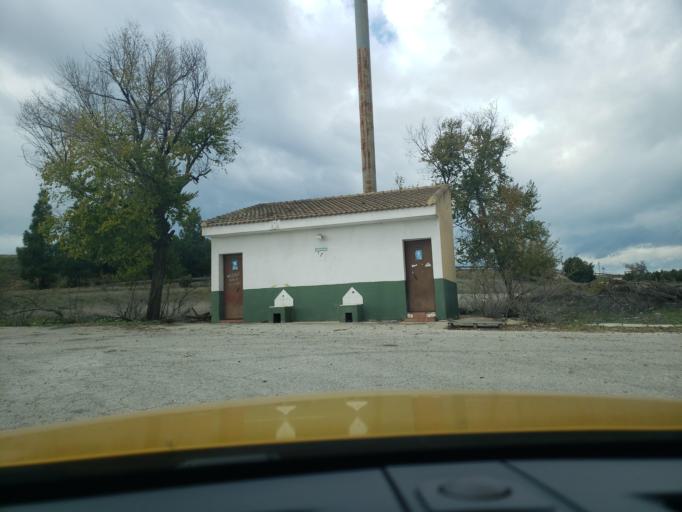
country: ES
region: Andalusia
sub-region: Provincia de Jaen
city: Guarroman
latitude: 38.1808
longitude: -3.6932
